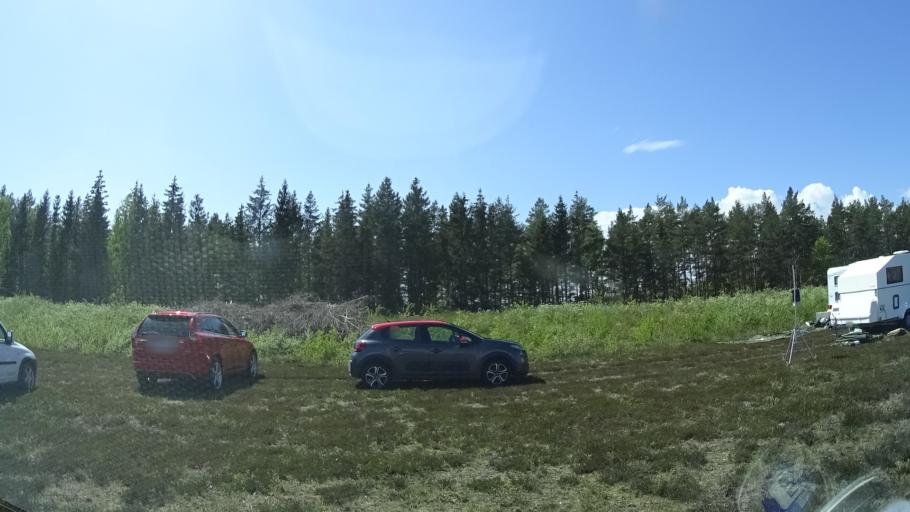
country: SE
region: Kalmar
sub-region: Vasterviks Kommun
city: Vaestervik
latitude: 57.7823
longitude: 16.5202
